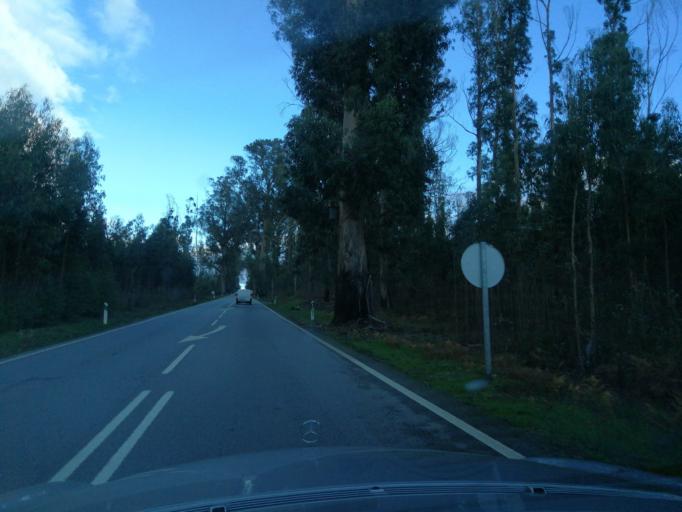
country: PT
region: Braga
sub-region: Esposende
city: Marinhas
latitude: 41.5728
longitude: -8.7156
